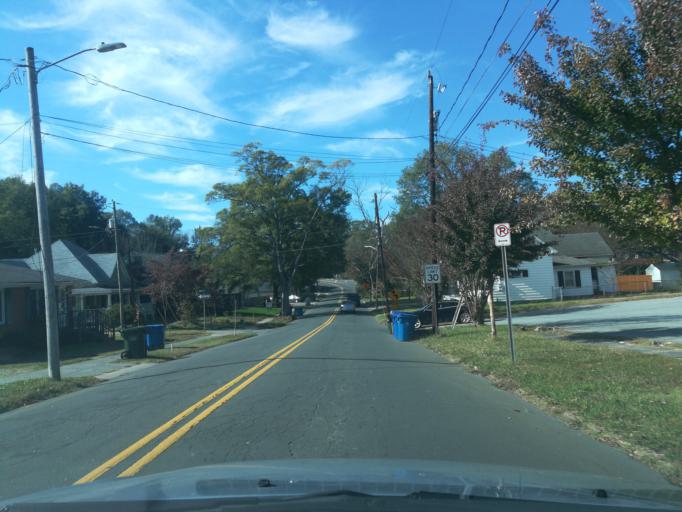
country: US
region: North Carolina
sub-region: Durham County
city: Durham
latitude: 35.9859
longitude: -78.8782
